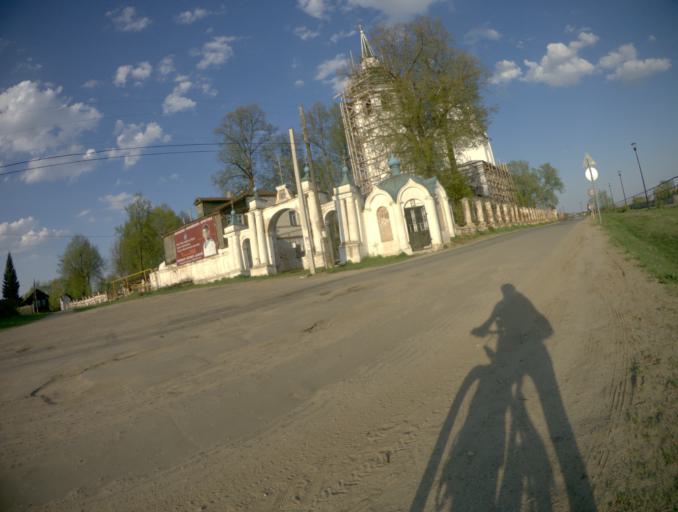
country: RU
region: Ivanovo
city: Yuzha
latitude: 56.5788
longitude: 41.8708
